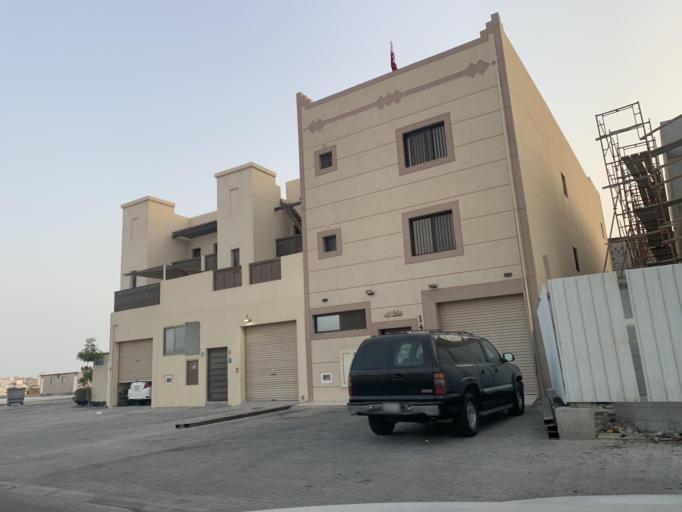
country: BH
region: Manama
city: Jidd Hafs
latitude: 26.2236
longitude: 50.4472
